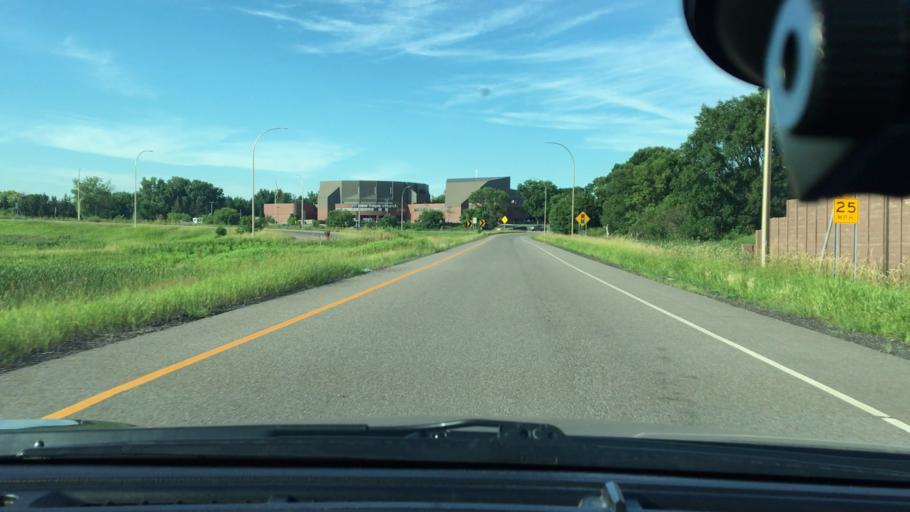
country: US
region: Minnesota
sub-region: Hennepin County
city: New Hope
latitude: 45.0317
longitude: -93.3996
